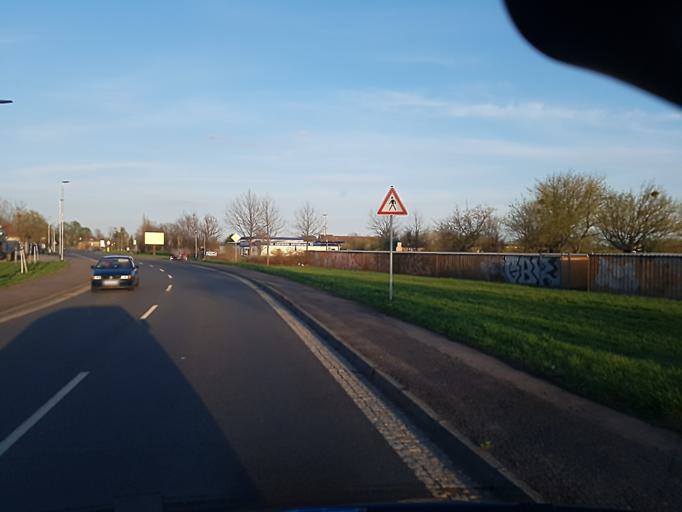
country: DE
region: Saxony
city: Zinna
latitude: 51.5650
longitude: 12.9714
